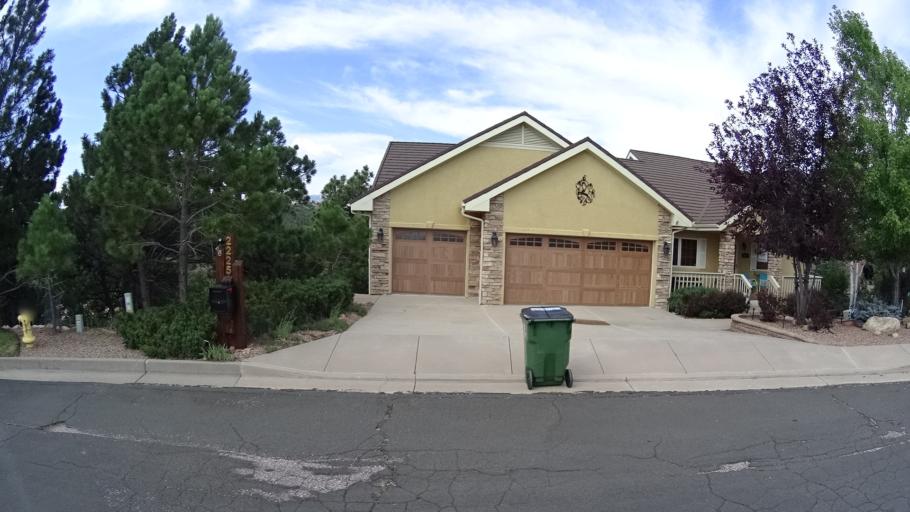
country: US
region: Colorado
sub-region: El Paso County
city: Air Force Academy
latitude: 38.9465
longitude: -104.8620
